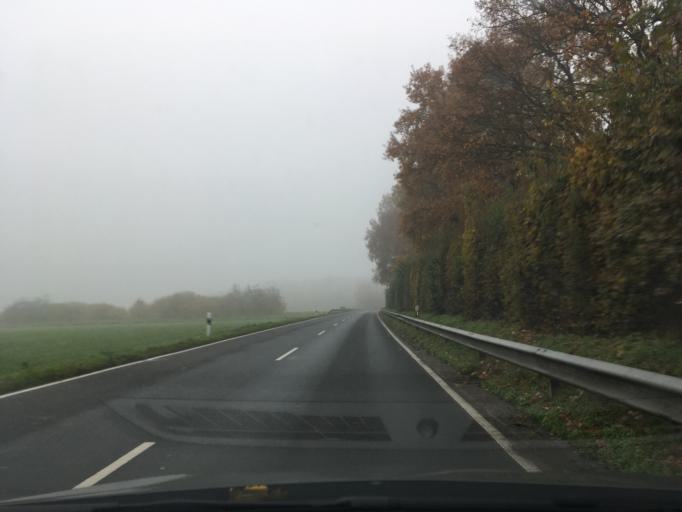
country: DE
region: North Rhine-Westphalia
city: Stadtlohn
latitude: 52.0715
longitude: 6.9268
